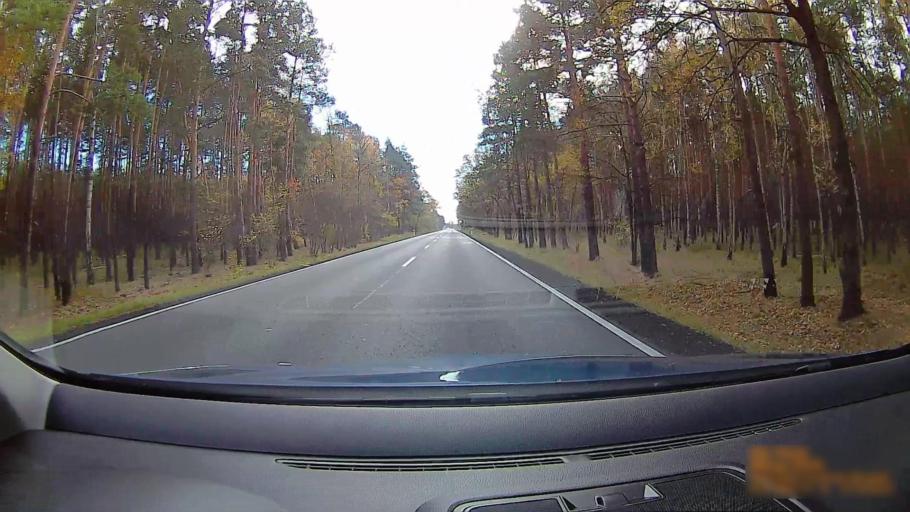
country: PL
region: Greater Poland Voivodeship
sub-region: Powiat ostrowski
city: Przygodzice
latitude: 51.4962
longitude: 17.8542
